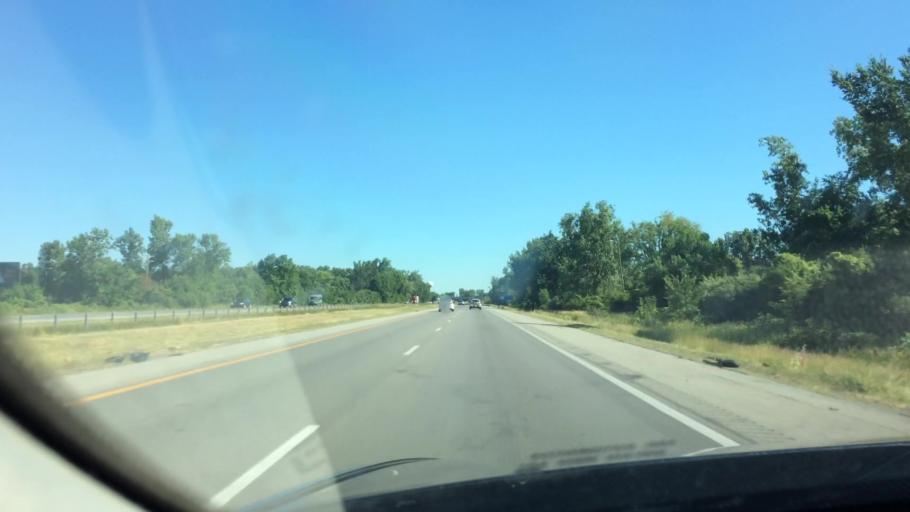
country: US
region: Michigan
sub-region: Washtenaw County
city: Milan
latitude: 42.0679
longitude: -83.6703
